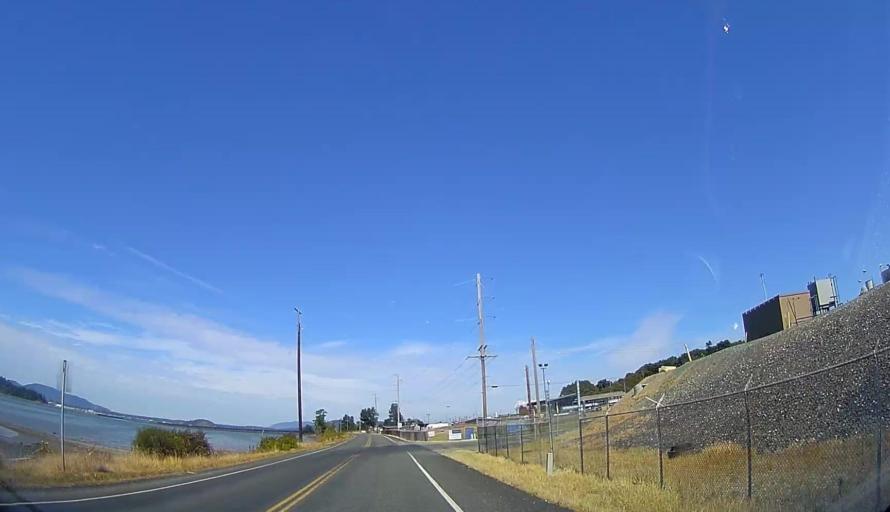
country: US
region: Washington
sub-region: Skagit County
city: Anacortes
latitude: 48.4707
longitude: -122.5708
